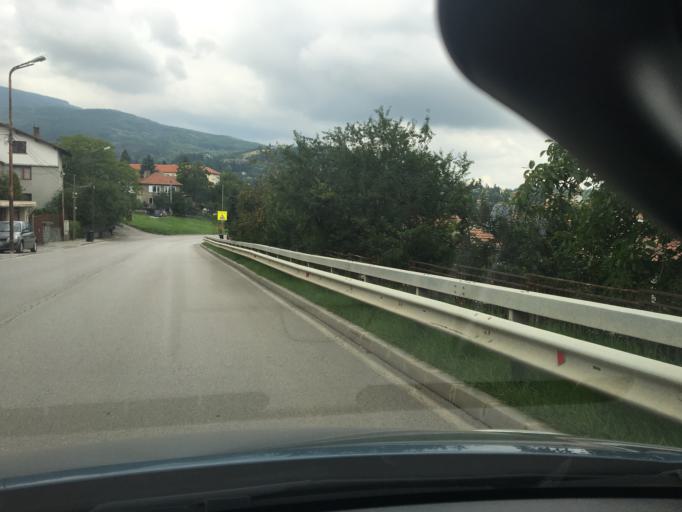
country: BG
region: Sofia-Capital
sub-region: Stolichna Obshtina
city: Sofia
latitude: 42.5821
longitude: 23.3602
